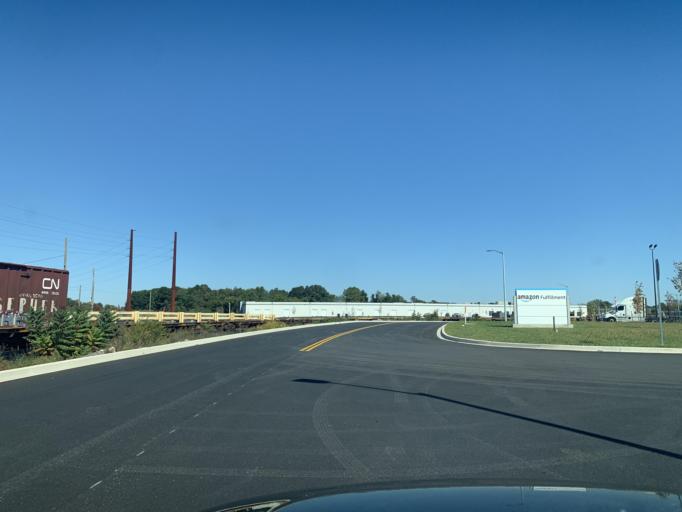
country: US
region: Maryland
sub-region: Baltimore County
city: Edgemere
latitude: 39.2330
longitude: -76.4787
